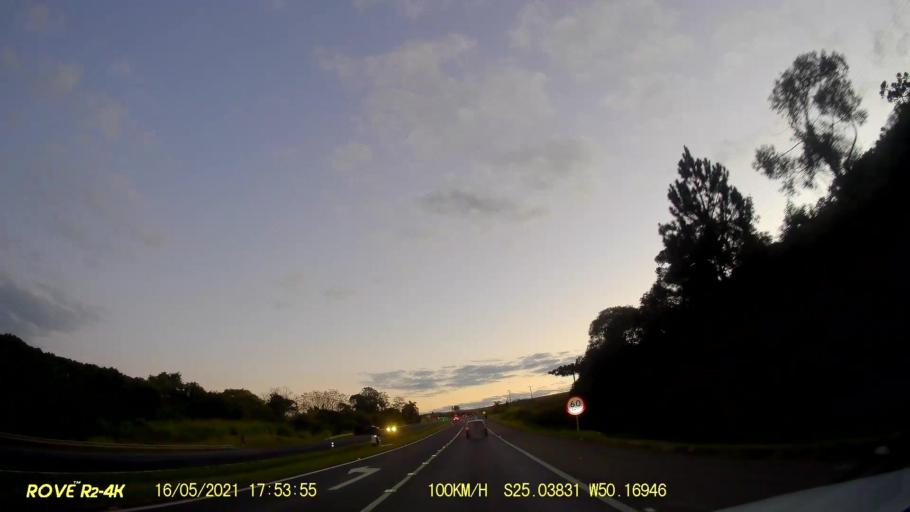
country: BR
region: Parana
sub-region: Ponta Grossa
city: Ponta Grossa
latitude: -25.0383
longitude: -50.1697
